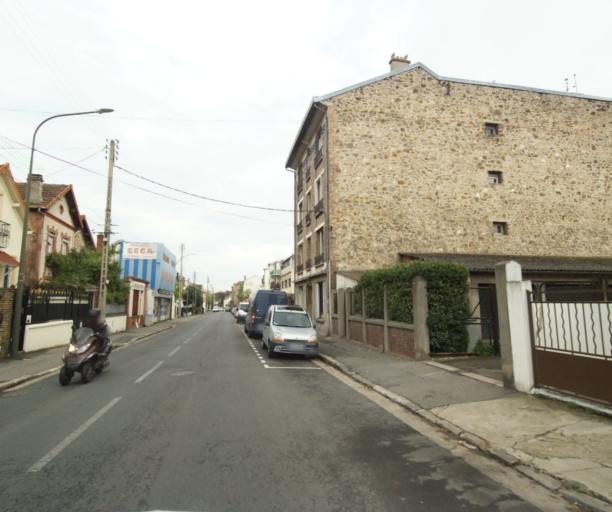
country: FR
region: Ile-de-France
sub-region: Departement du Val-d'Oise
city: Argenteuil
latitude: 48.9513
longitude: 2.2439
